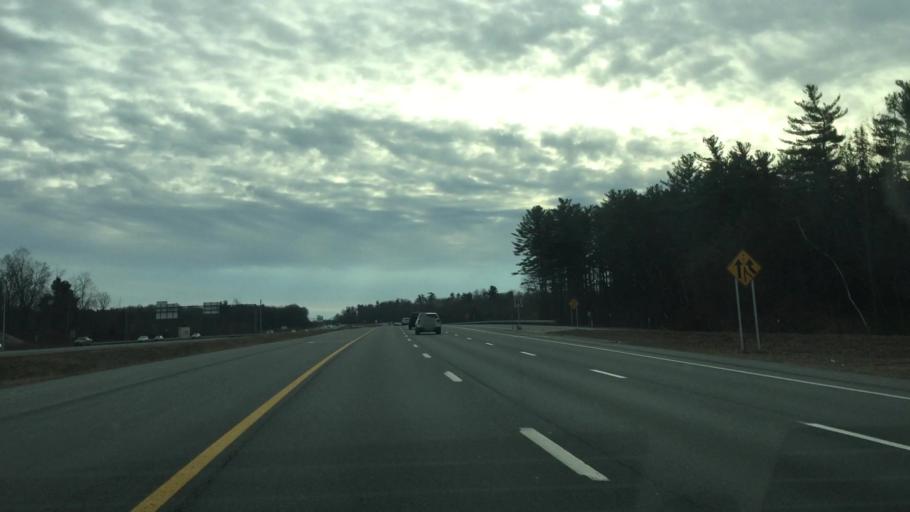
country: US
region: New Hampshire
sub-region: Rockingham County
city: Windham
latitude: 42.8048
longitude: -71.2714
